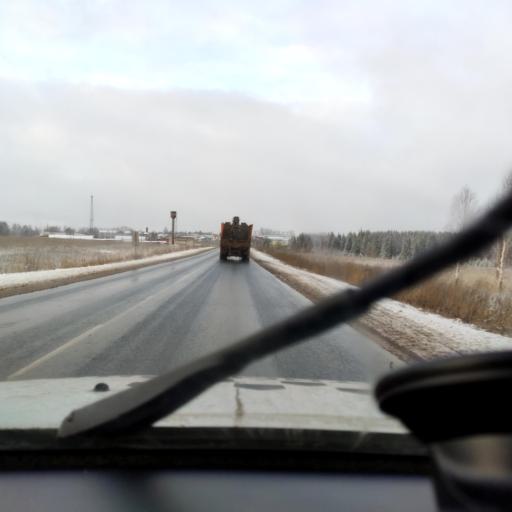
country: RU
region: Perm
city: Nytva
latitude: 57.9448
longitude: 55.3643
